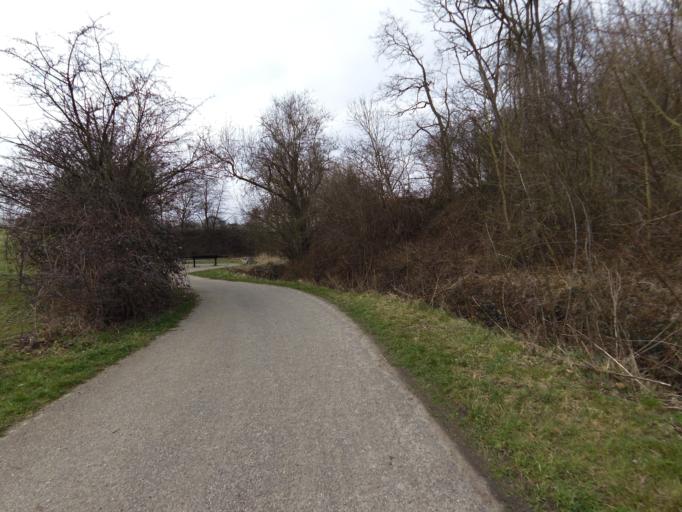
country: NL
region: Limburg
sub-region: Gemeente Kerkrade
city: Kerkrade
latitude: 50.8846
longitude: 6.0663
